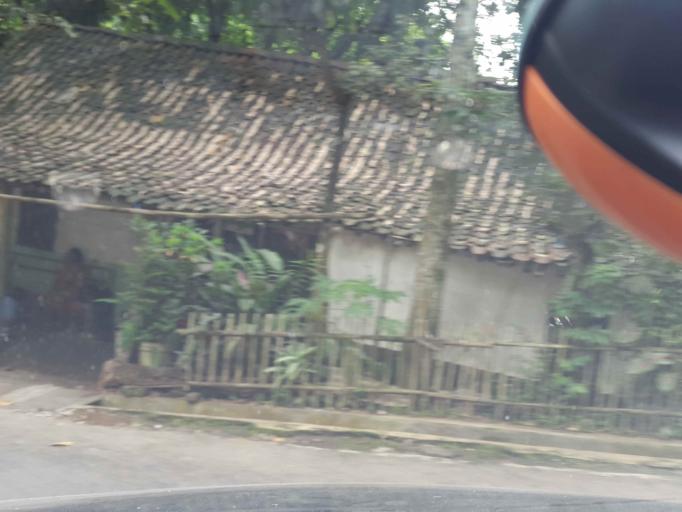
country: ID
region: Central Java
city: Salatiga
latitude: -7.3209
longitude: 110.5169
